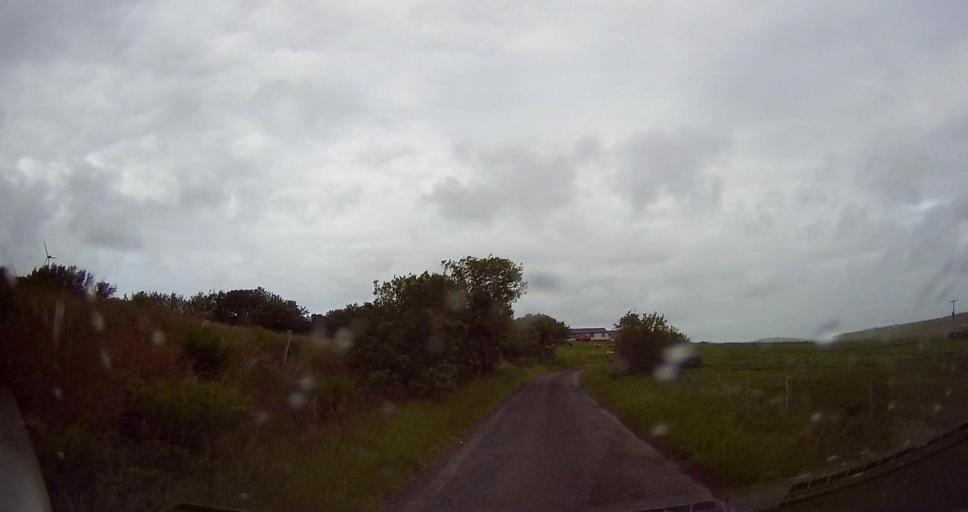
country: GB
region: Scotland
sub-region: Orkney Islands
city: Stromness
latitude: 58.9097
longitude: -3.3206
